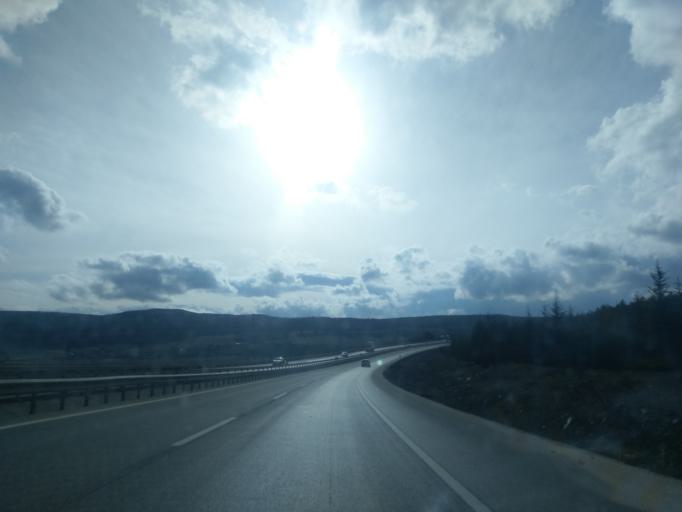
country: TR
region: Kuetahya
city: Sabuncu
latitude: 39.5736
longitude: 30.1169
